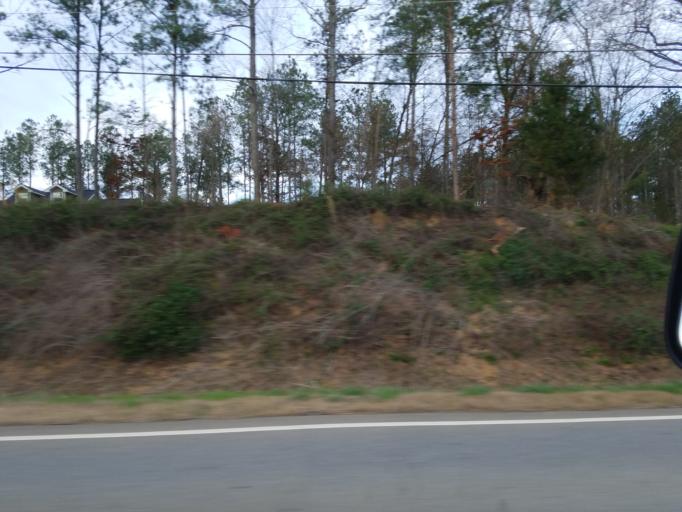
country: US
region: Georgia
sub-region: Bartow County
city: Rydal
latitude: 34.4479
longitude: -84.8029
